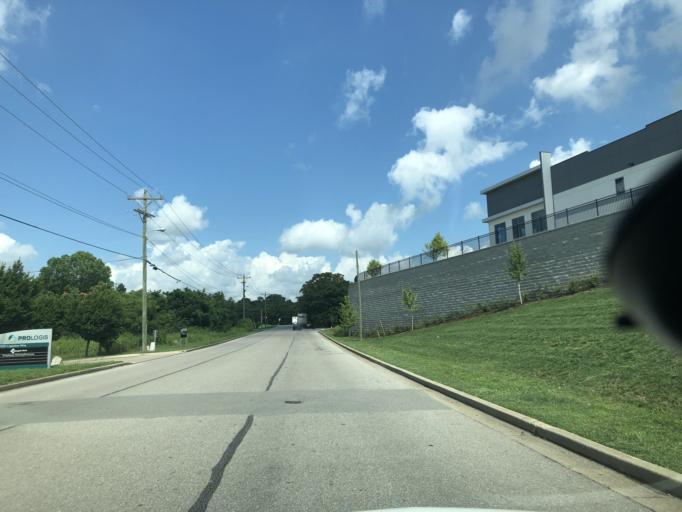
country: US
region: Tennessee
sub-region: Rutherford County
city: La Vergne
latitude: 36.0291
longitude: -86.6094
